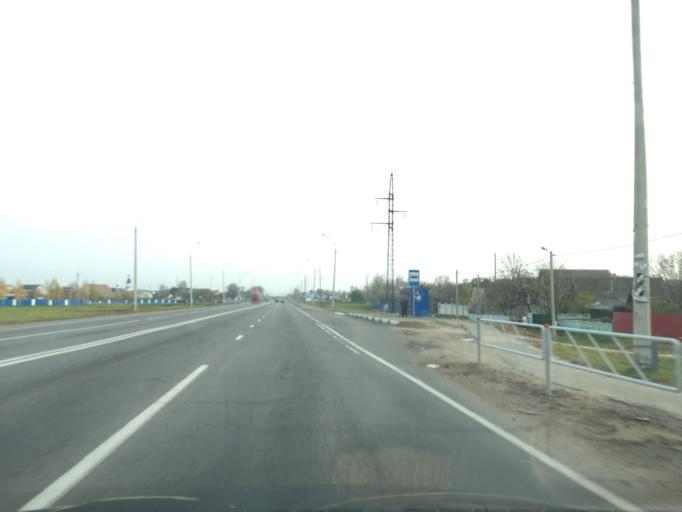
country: BY
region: Gomel
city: Kastsyukowka
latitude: 52.5132
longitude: 30.9397
